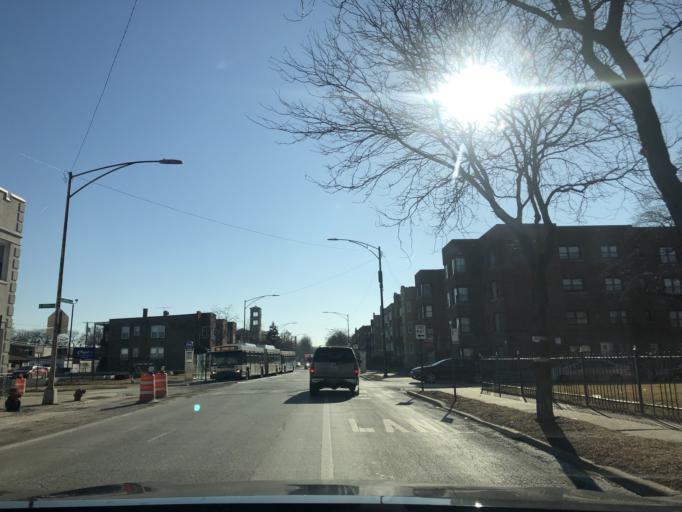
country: US
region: Indiana
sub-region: Lake County
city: Whiting
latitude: 41.7556
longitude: -87.5761
